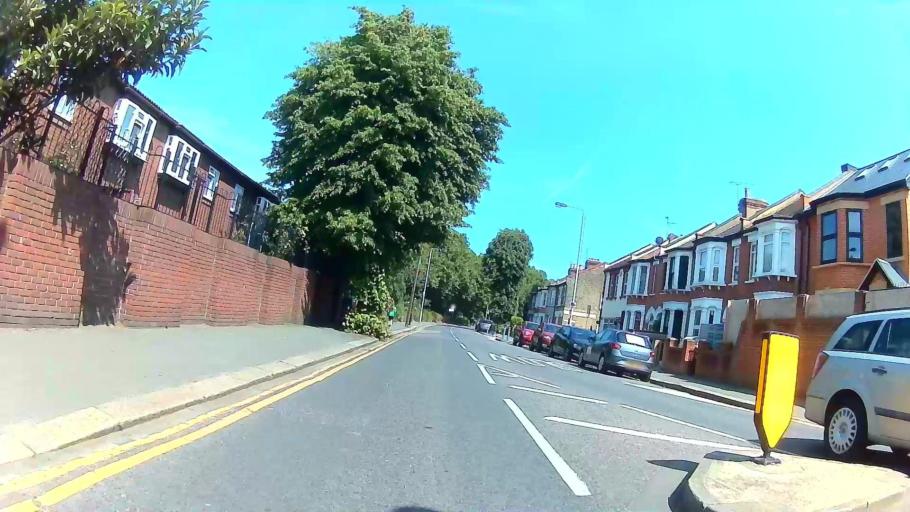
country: GB
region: England
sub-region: Greater London
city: East Ham
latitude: 51.5594
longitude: 0.0142
